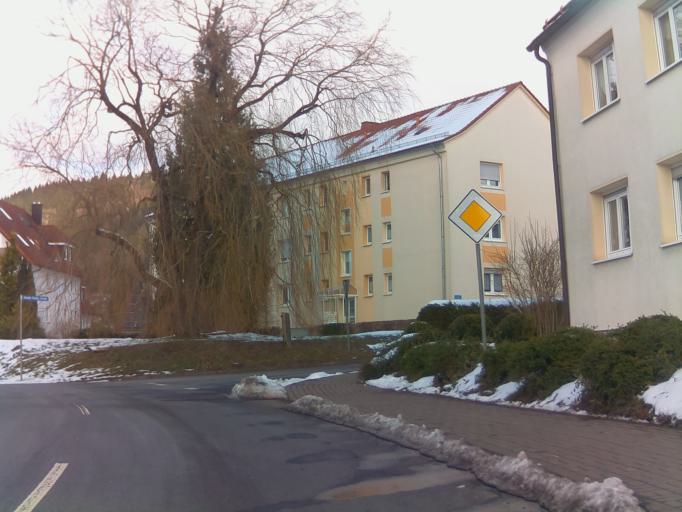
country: DE
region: Thuringia
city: Suhl
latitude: 50.6123
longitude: 10.6721
